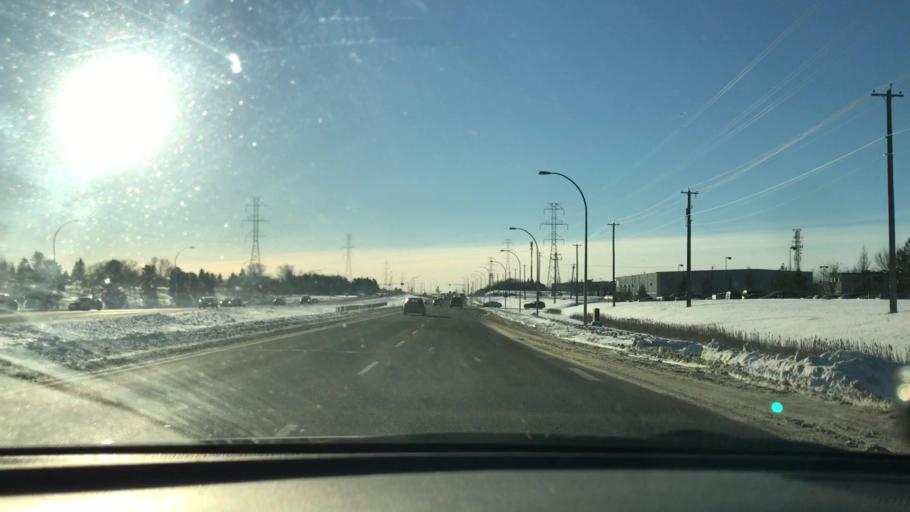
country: CA
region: Alberta
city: Edmonton
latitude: 53.4564
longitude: -113.4669
